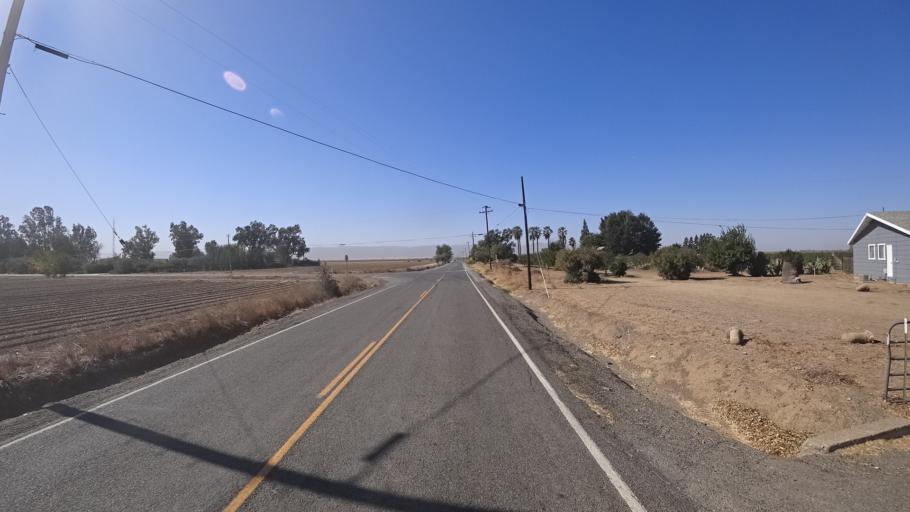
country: US
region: California
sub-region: Yolo County
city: Winters
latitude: 38.5839
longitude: -121.9324
